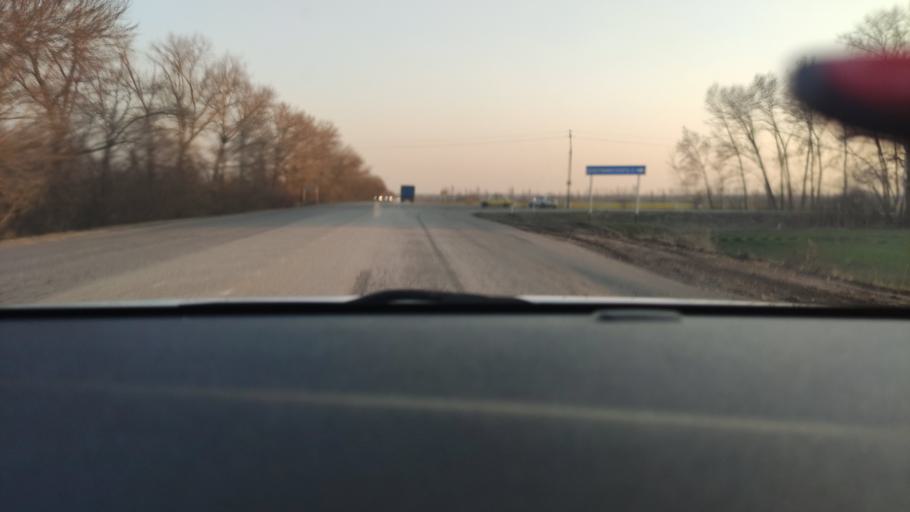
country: RU
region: Voronezj
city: Maslovka
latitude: 51.4377
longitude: 39.3022
